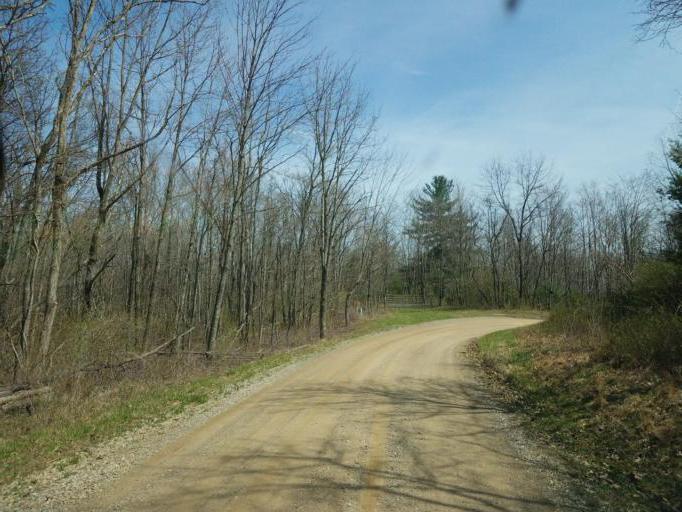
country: US
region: Ohio
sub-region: Knox County
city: Oak Hill
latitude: 40.3847
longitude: -82.1673
